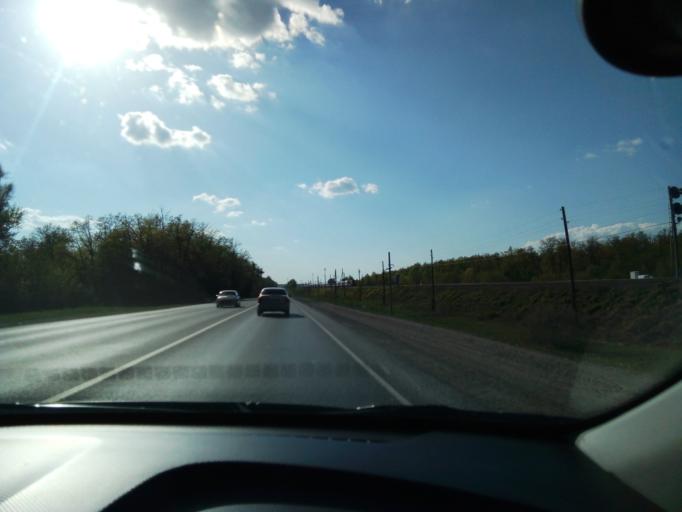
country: RU
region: Chuvashia
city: Novyye Lapsary
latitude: 56.0738
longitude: 47.2072
